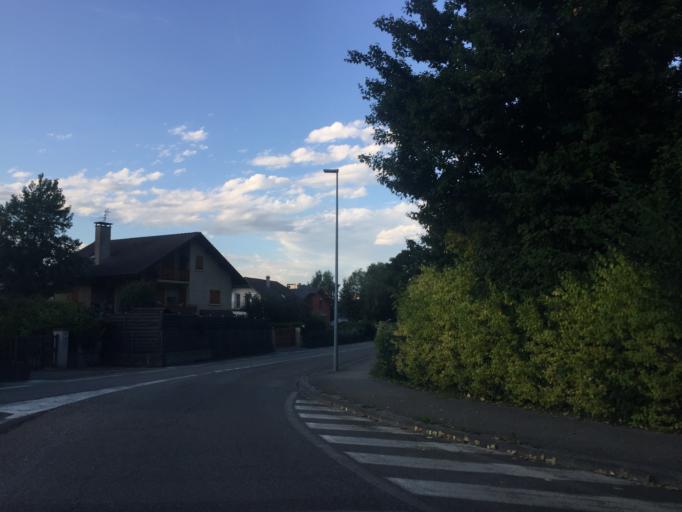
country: FR
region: Rhone-Alpes
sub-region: Departement de la Savoie
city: La Motte-Servolex
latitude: 45.5910
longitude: 5.8709
